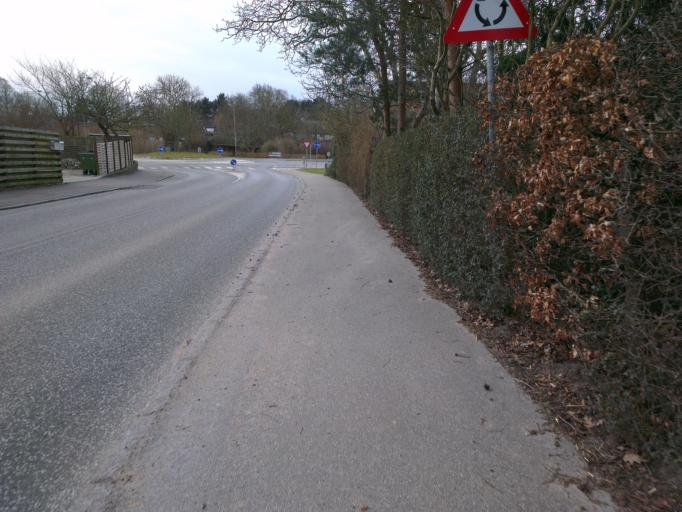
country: DK
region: Capital Region
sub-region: Frederikssund Kommune
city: Jaegerspris
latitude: 55.8076
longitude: 11.9827
